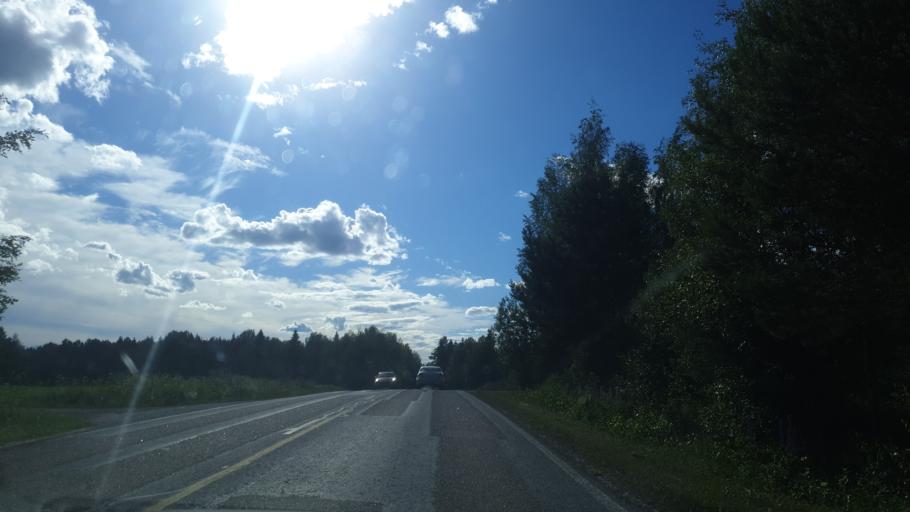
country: FI
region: Southern Savonia
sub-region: Mikkeli
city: Pertunmaa
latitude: 61.5227
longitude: 26.5593
